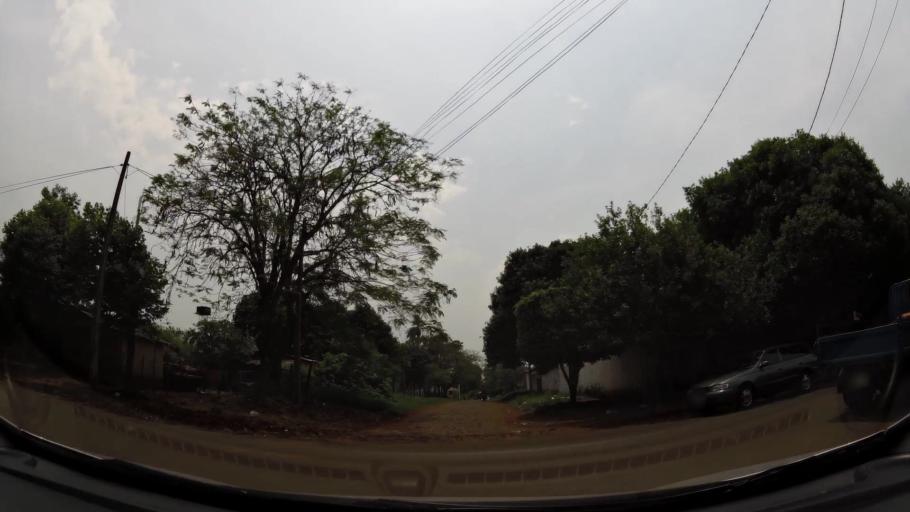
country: BR
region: Parana
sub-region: Foz Do Iguacu
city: Foz do Iguacu
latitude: -25.5670
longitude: -54.6105
